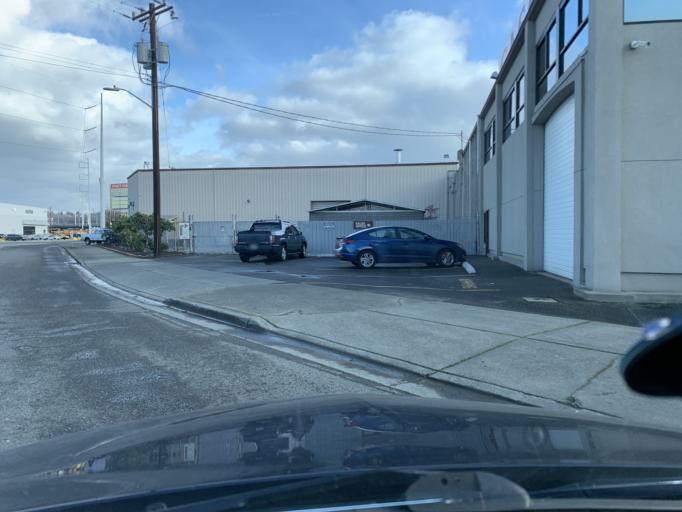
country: US
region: Washington
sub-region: King County
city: Seattle
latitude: 47.5623
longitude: -122.3391
